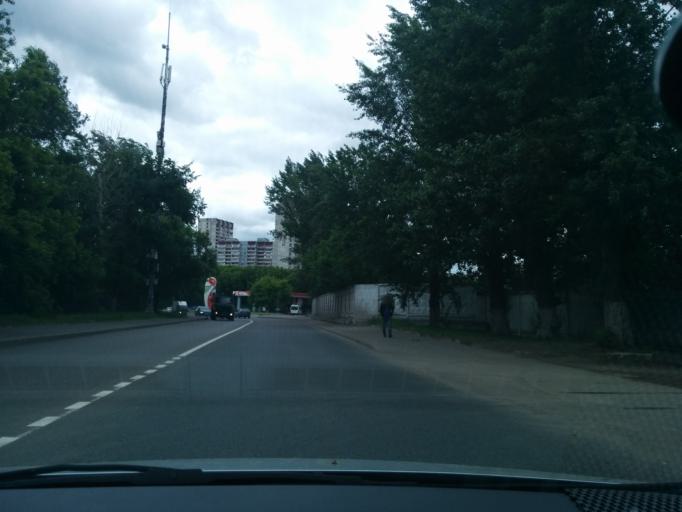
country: RU
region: Moscow
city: Tekstil'shchiki
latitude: 55.6949
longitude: 37.7281
